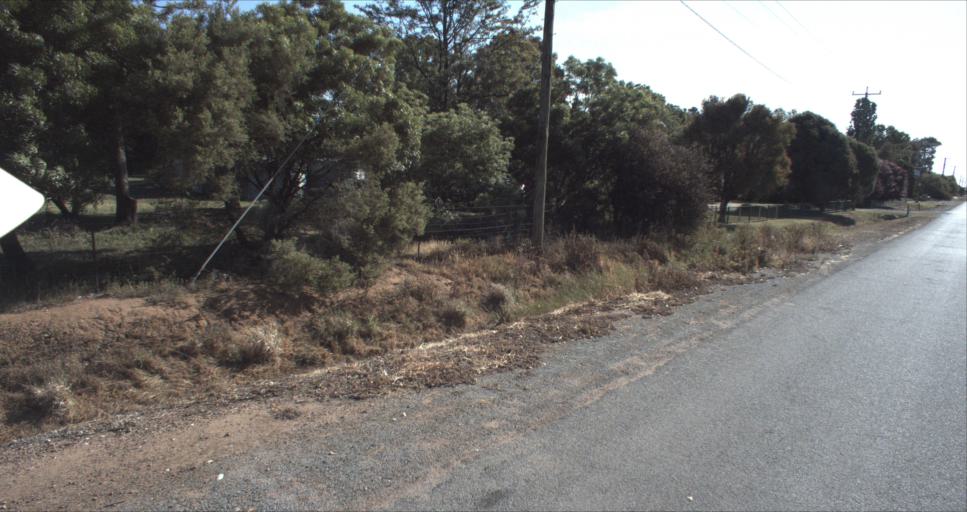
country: AU
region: New South Wales
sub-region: Leeton
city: Leeton
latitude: -34.5407
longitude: 146.4153
